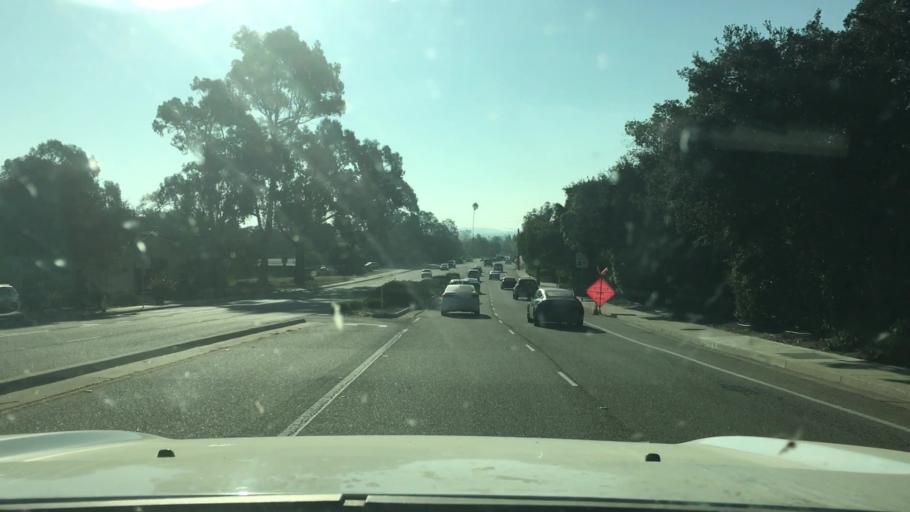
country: US
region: California
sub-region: San Luis Obispo County
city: San Luis Obispo
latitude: 35.2602
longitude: -120.6492
